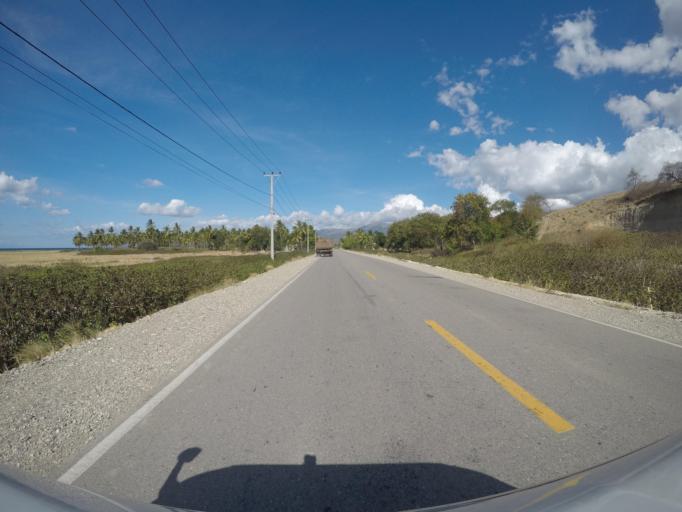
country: TL
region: Baucau
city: Baucau
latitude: -8.4762
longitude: 126.5395
